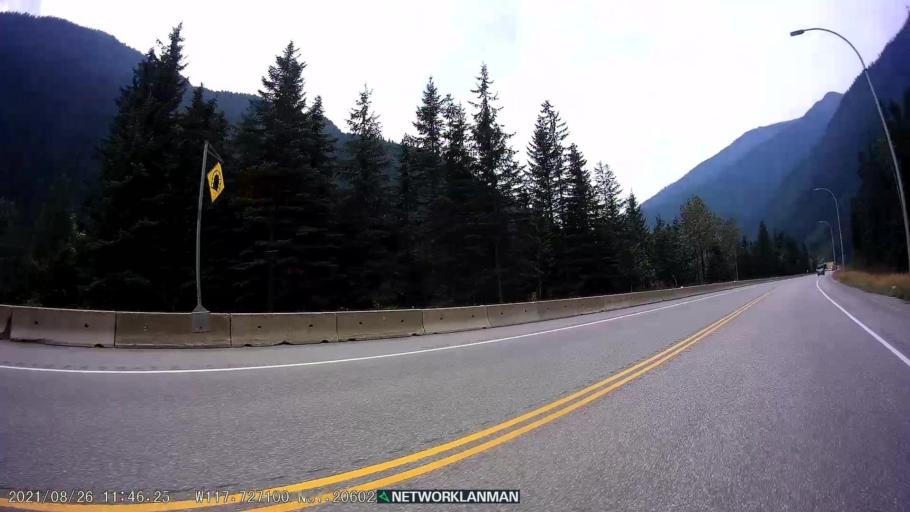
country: CA
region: British Columbia
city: Revelstoke
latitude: 51.2061
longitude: -117.7275
